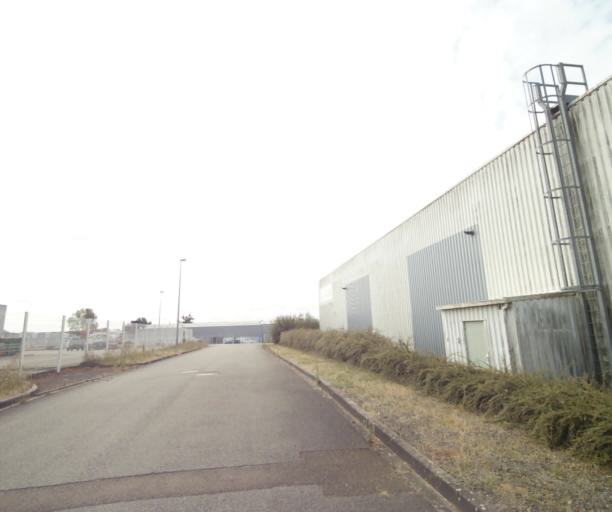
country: FR
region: Pays de la Loire
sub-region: Departement de la Sarthe
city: Solesmes
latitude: 47.8202
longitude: -0.3068
